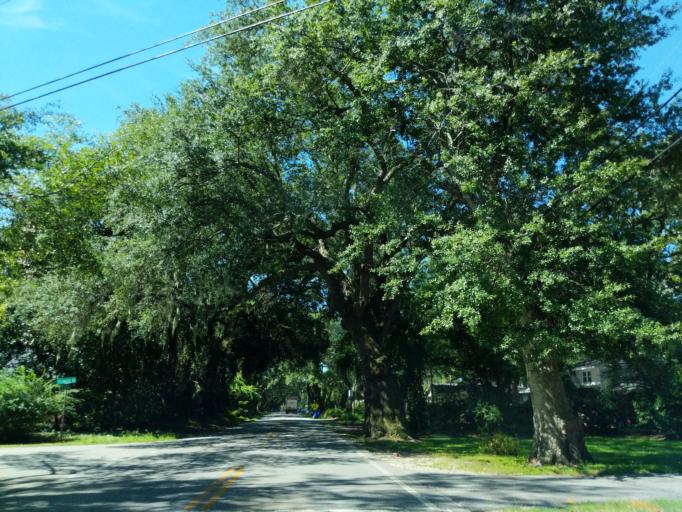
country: US
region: South Carolina
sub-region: Charleston County
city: Charleston
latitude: 32.7353
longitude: -79.9241
